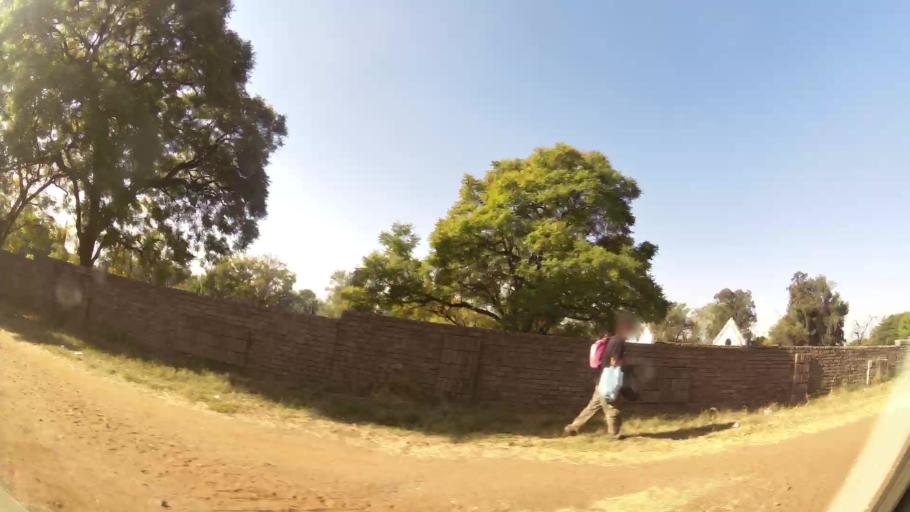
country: ZA
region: North-West
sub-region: Bojanala Platinum District Municipality
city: Rustenburg
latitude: -25.6761
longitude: 27.2446
